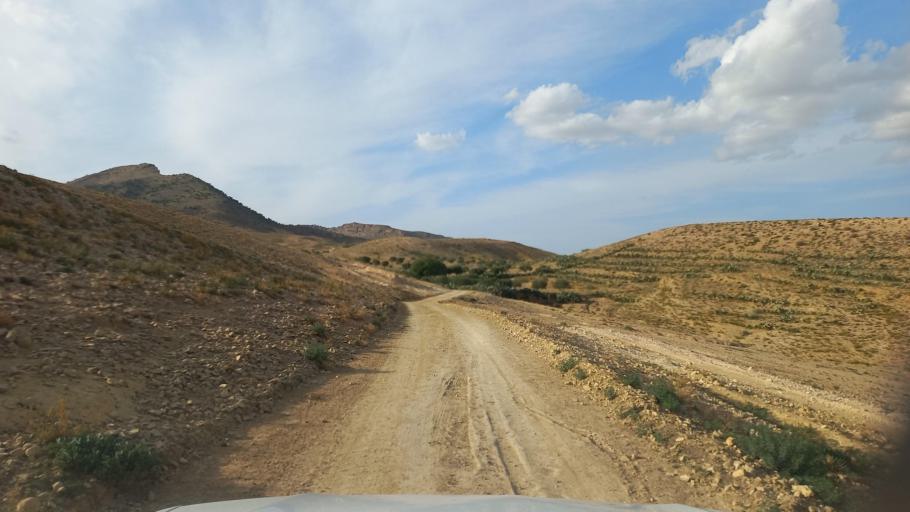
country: TN
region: Al Qasrayn
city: Sbiba
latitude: 35.4562
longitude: 9.0833
